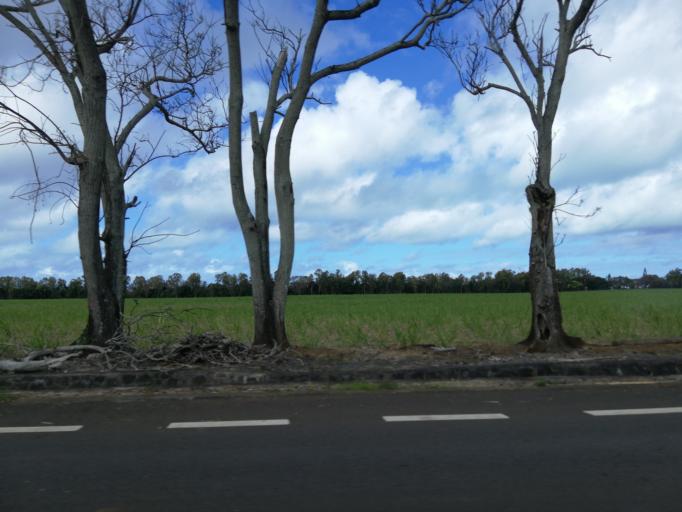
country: MU
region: Grand Port
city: Mahebourg
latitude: -20.3795
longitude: 57.6984
